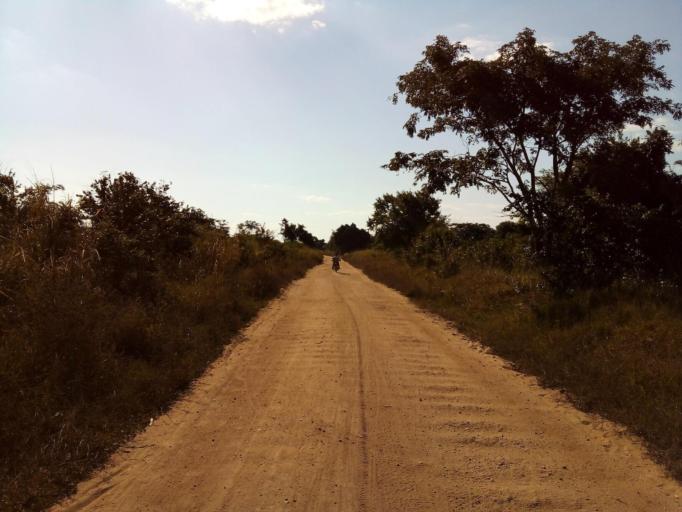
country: MZ
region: Zambezia
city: Quelimane
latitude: -17.5500
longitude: 36.6295
